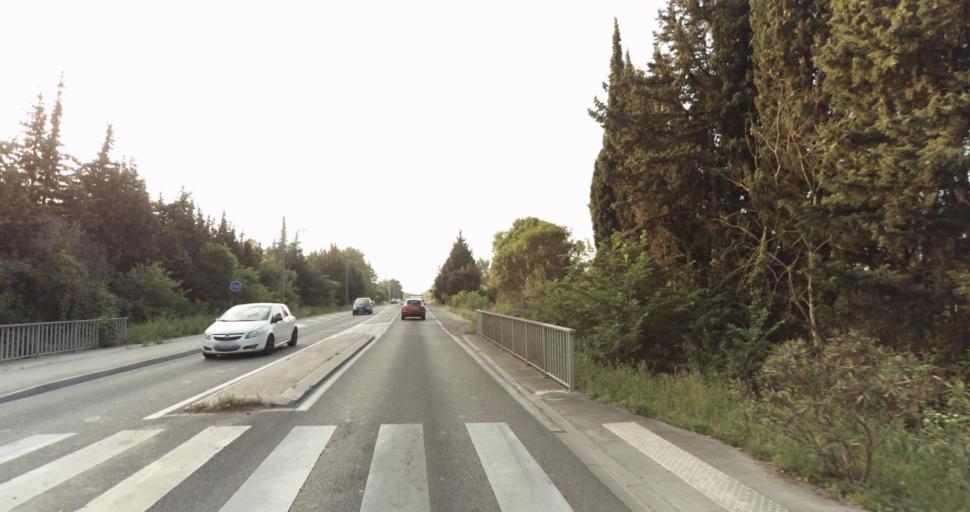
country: FR
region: Languedoc-Roussillon
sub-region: Departement du Gard
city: Caissargues
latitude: 43.8205
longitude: 4.3863
